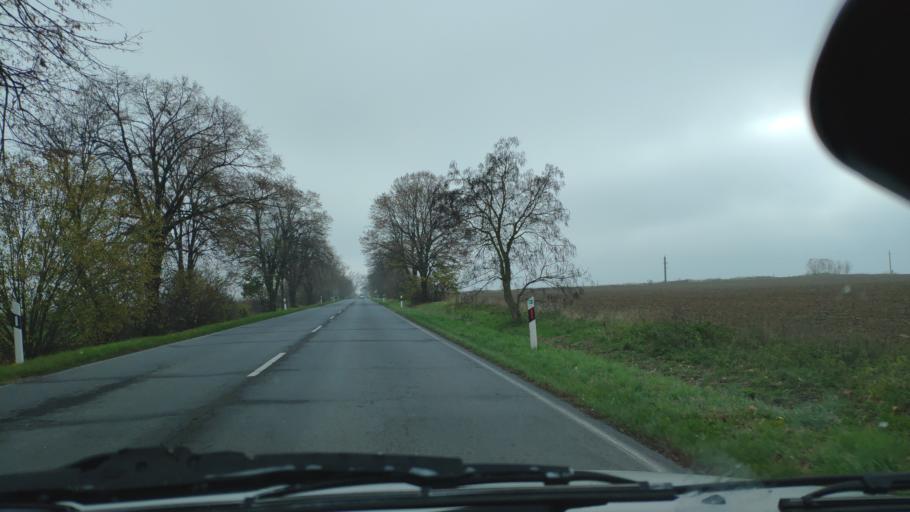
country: HU
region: Zala
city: Zalakomar
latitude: 46.5675
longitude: 17.2620
